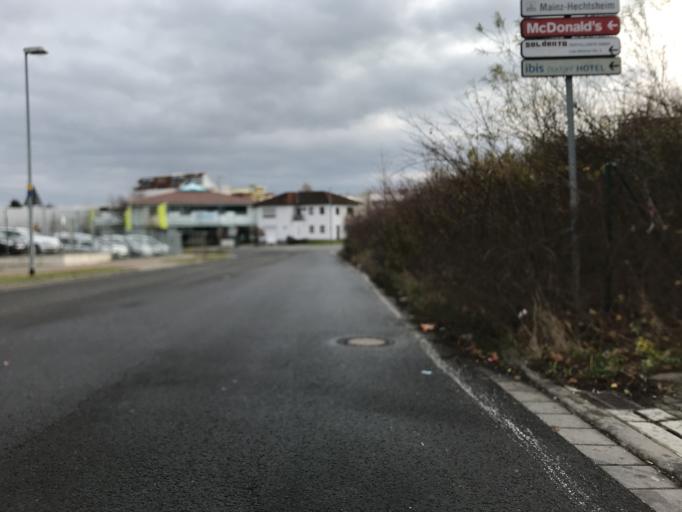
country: DE
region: Rheinland-Pfalz
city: Mainz
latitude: 49.9637
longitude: 8.2539
